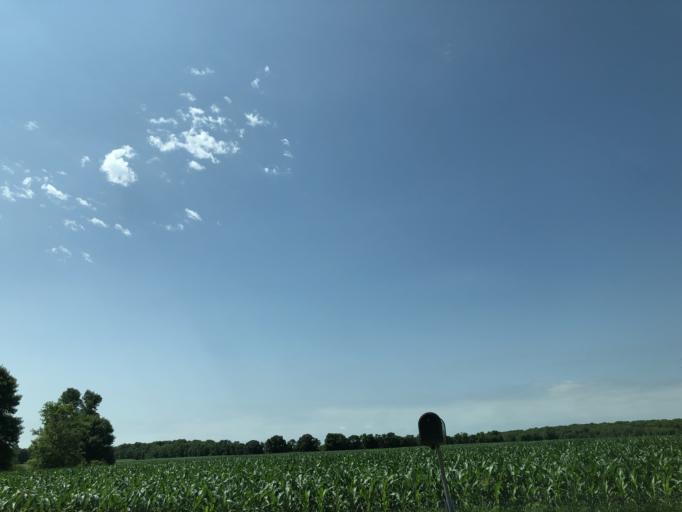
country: US
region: Minnesota
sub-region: Douglas County
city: Alexandria
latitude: 45.9388
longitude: -95.3792
